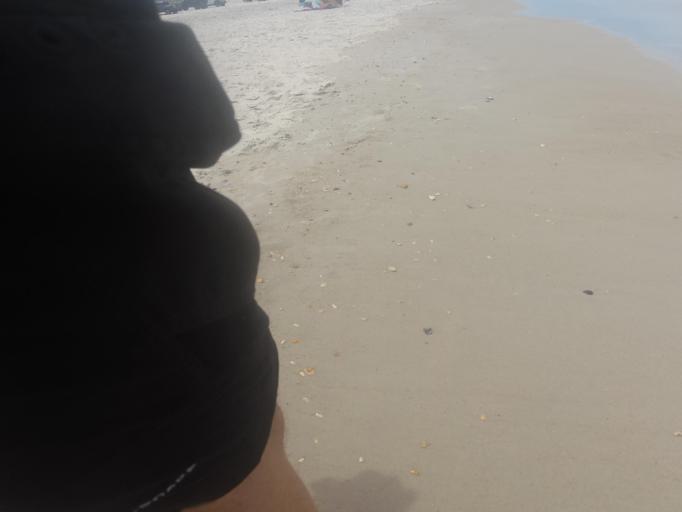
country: US
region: Florida
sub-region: Saint Johns County
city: Saint Augustine Beach
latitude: 29.8402
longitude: -81.2636
